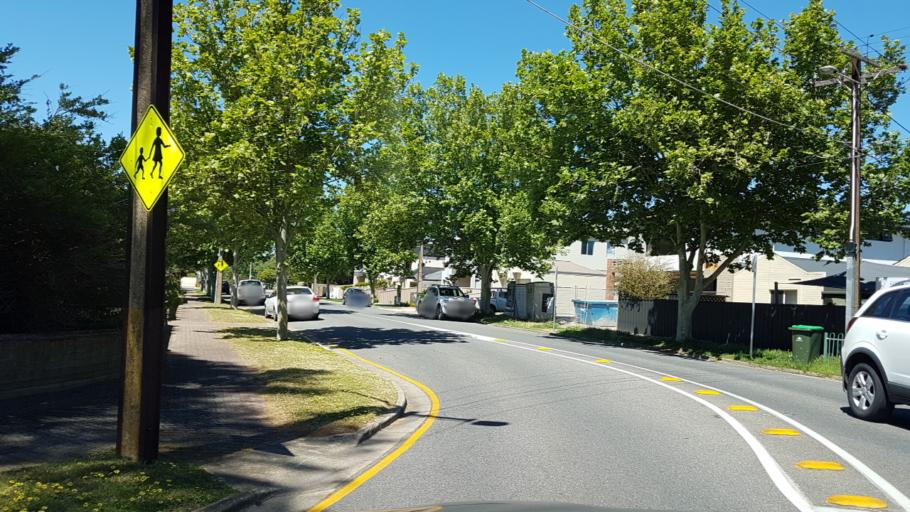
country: AU
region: South Australia
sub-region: Holdfast Bay
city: Glenelg East
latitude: -34.9687
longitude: 138.5204
